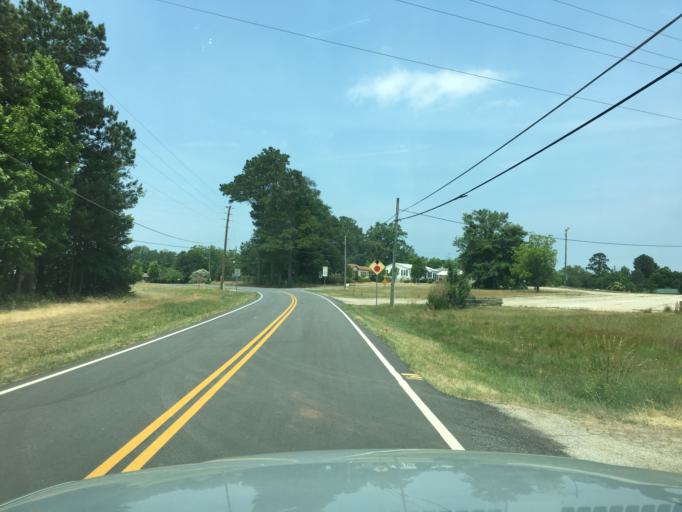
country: US
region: Georgia
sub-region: Hart County
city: Hartwell
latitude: 34.3494
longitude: -82.9167
